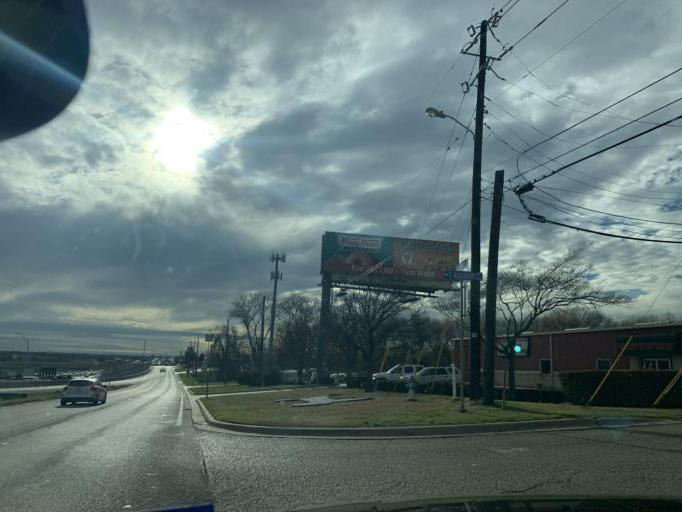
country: US
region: Texas
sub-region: Dallas County
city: Duncanville
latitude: 32.6353
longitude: -96.8985
